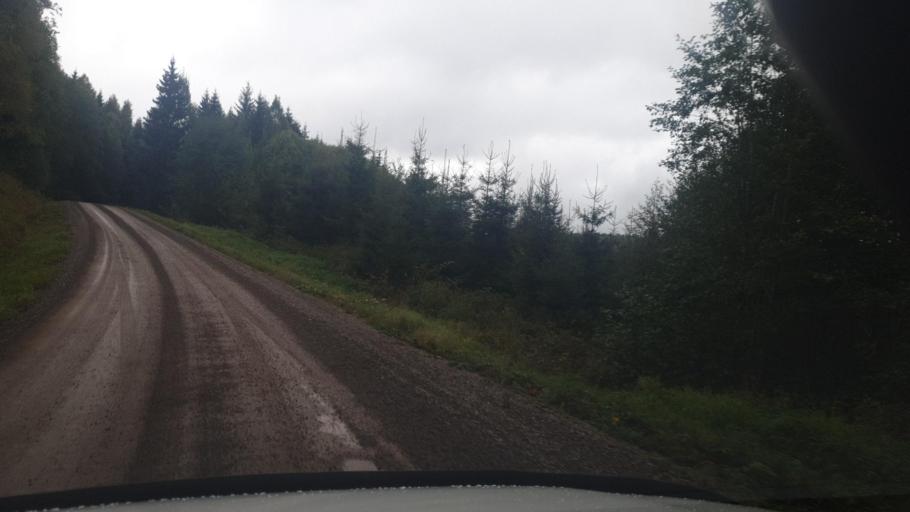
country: SE
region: Vaermland
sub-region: Arvika Kommun
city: Arvika
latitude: 60.0075
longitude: 12.6578
